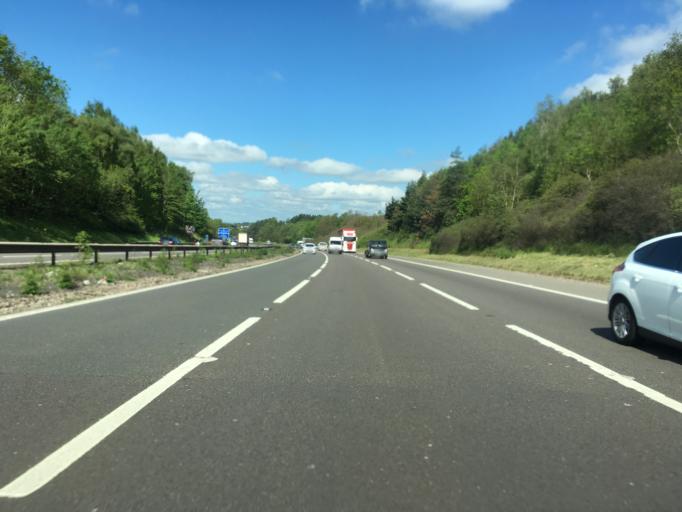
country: GB
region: England
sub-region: Worcestershire
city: Barnt Green
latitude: 52.3566
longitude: -2.0197
